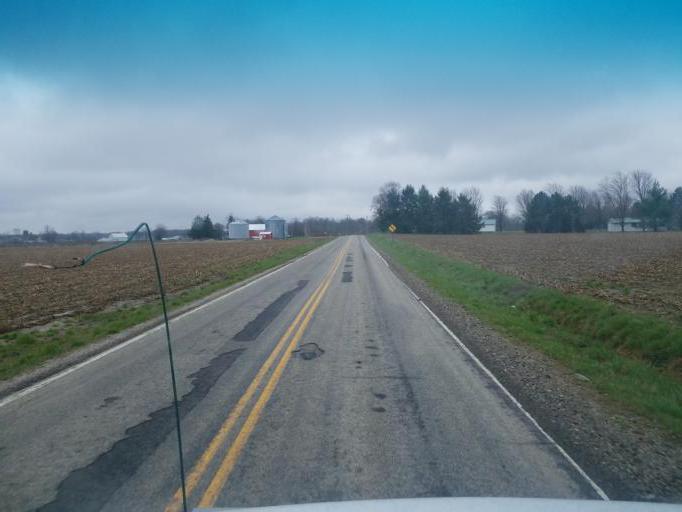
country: US
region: Ohio
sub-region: Richland County
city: Shelby
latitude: 40.9205
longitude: -82.6418
